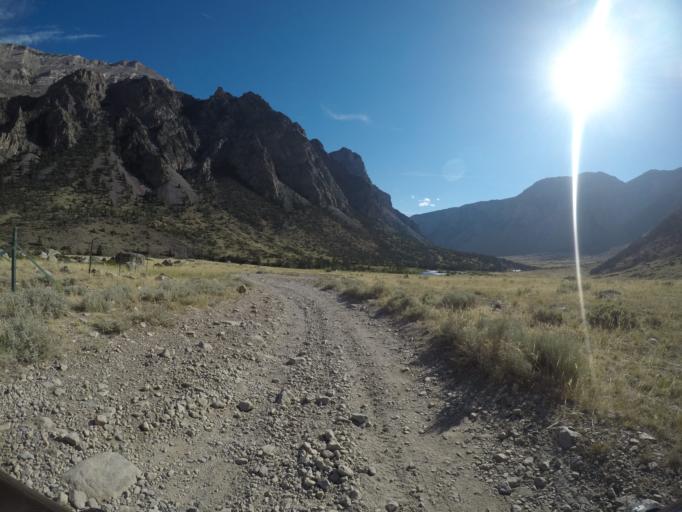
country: US
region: Montana
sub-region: Carbon County
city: Red Lodge
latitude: 44.8443
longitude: -109.3166
